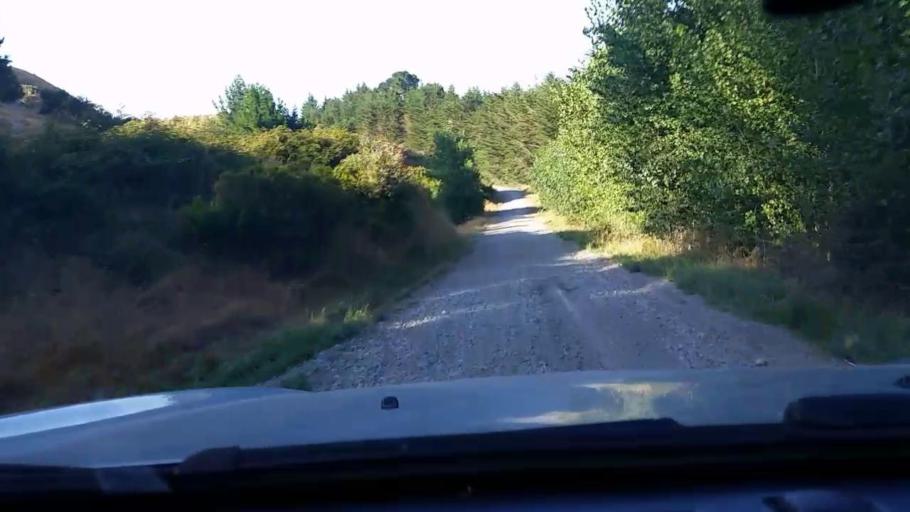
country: NZ
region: Waikato
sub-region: Taupo District
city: Taupo
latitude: -38.4856
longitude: 176.2106
